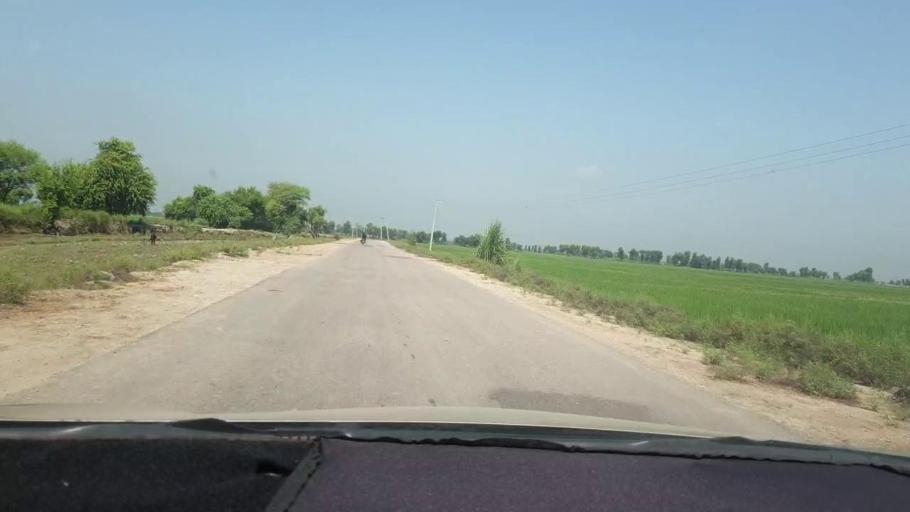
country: PK
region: Sindh
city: Miro Khan
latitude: 27.7665
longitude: 68.0710
